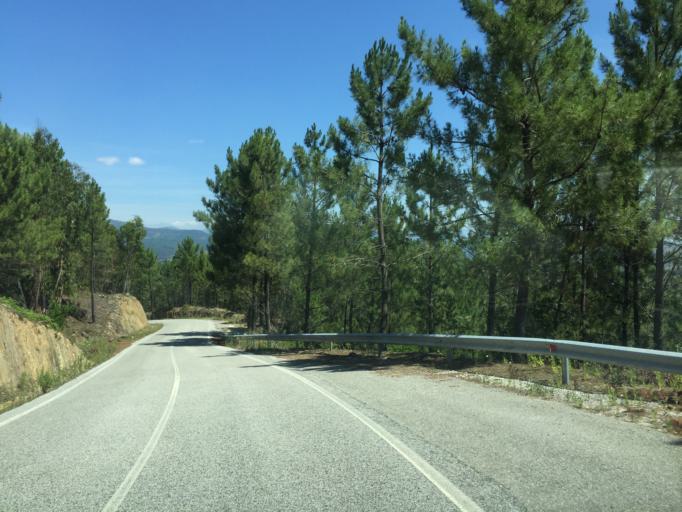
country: PT
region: Castelo Branco
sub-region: Oleiros
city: Oleiros
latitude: 39.9916
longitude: -7.8423
